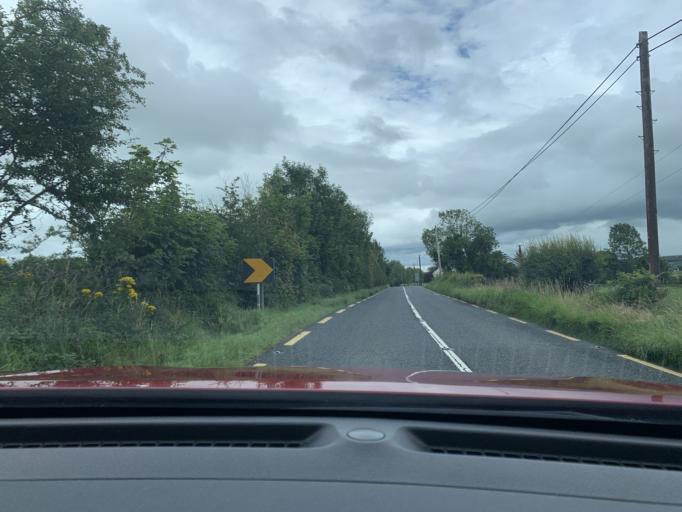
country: IE
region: Ulster
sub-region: County Donegal
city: Convoy
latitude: 54.7977
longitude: -7.6751
